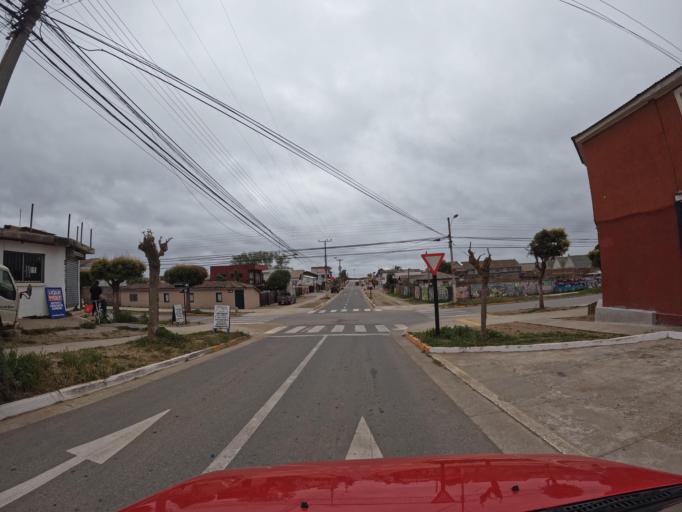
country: CL
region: O'Higgins
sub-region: Provincia de Colchagua
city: Santa Cruz
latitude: -34.3865
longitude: -72.0061
